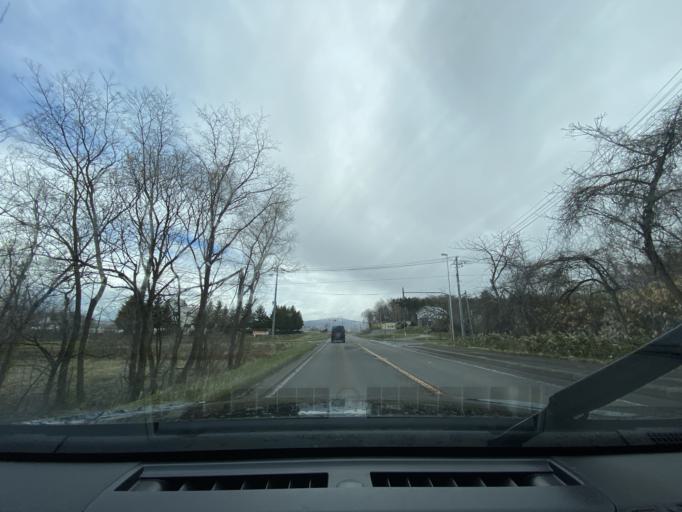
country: JP
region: Hokkaido
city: Fukagawa
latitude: 43.7024
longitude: 142.0767
